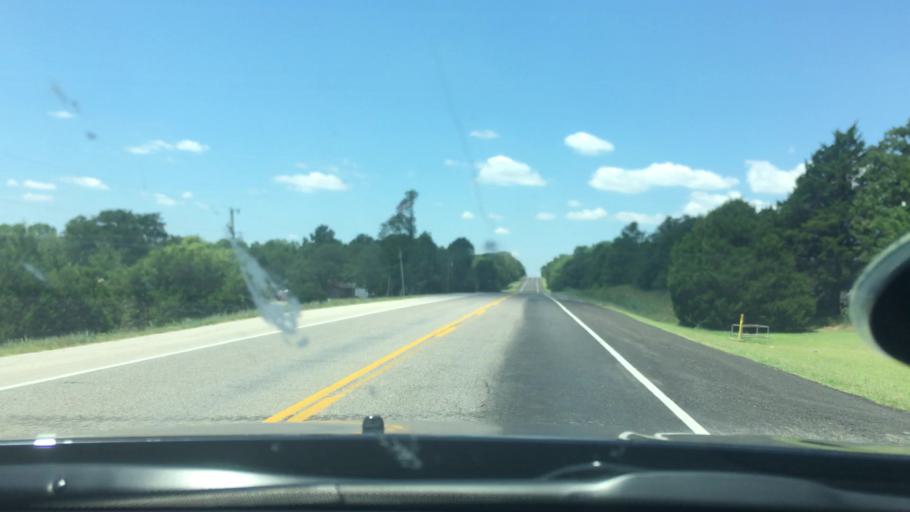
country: US
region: Oklahoma
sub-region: Carter County
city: Dickson
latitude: 34.1873
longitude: -96.9415
